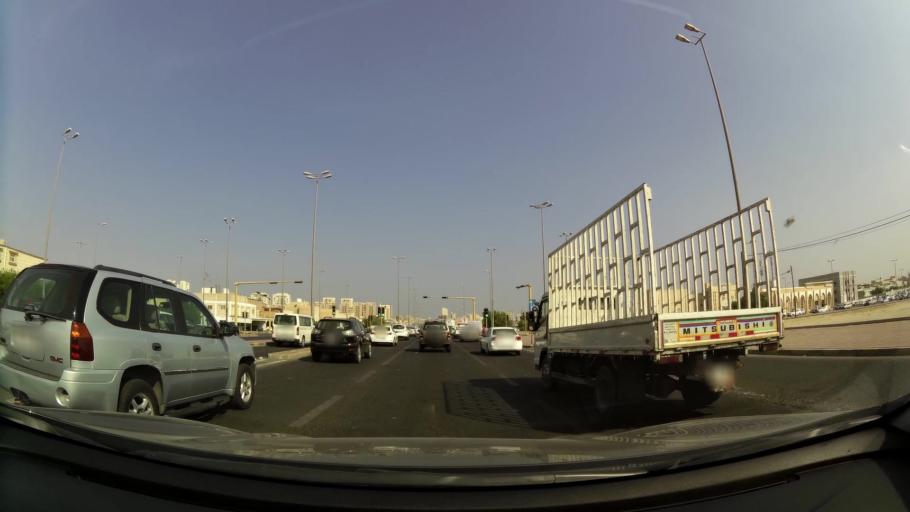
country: KW
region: Al Ahmadi
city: Ar Riqqah
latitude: 29.1352
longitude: 48.1087
